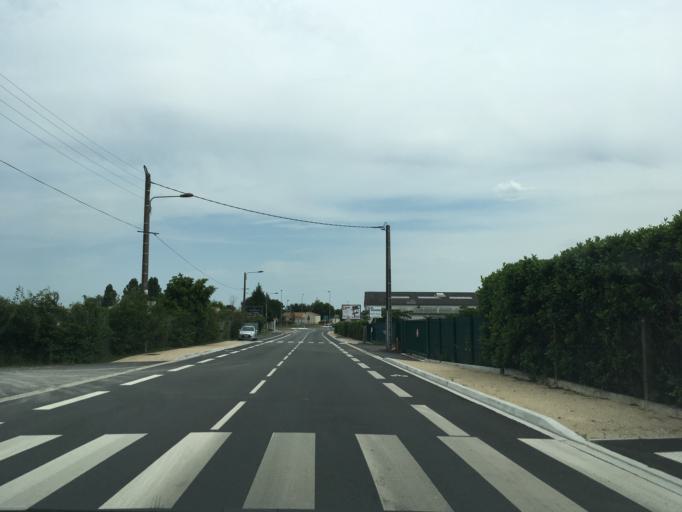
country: FR
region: Poitou-Charentes
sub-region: Departement des Deux-Sevres
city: Bessines
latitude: 46.3149
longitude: -0.5012
